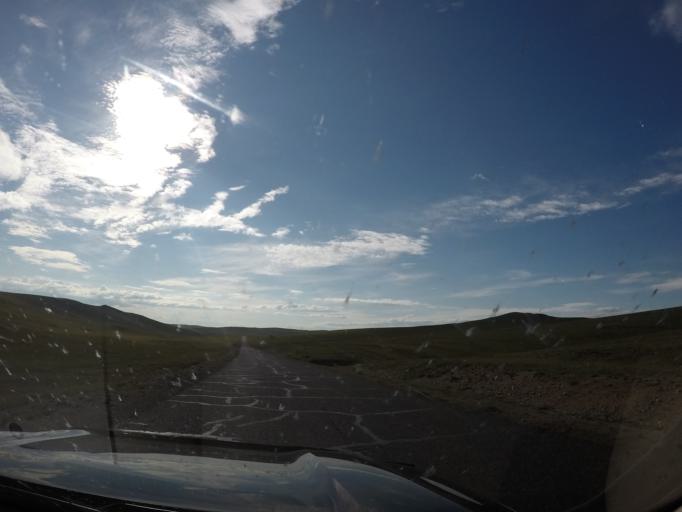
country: MN
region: Hentiy
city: Modot
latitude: 47.8056
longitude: 108.7333
